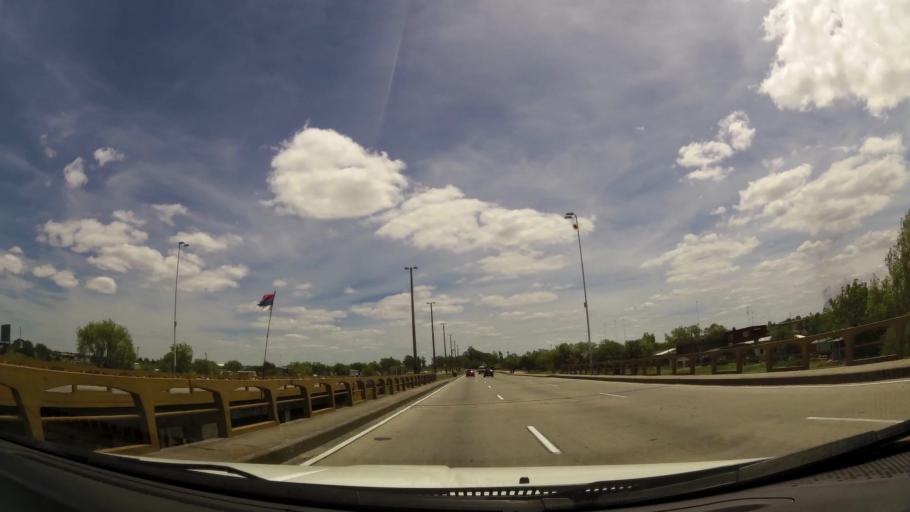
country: UY
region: Montevideo
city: Montevideo
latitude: -34.8685
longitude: -56.2450
